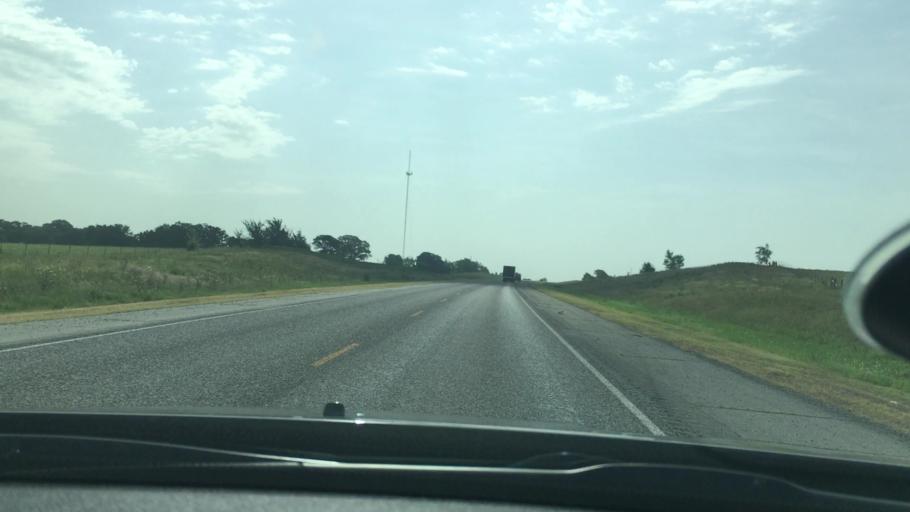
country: US
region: Oklahoma
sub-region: Coal County
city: Coalgate
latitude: 34.5992
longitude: -96.3190
